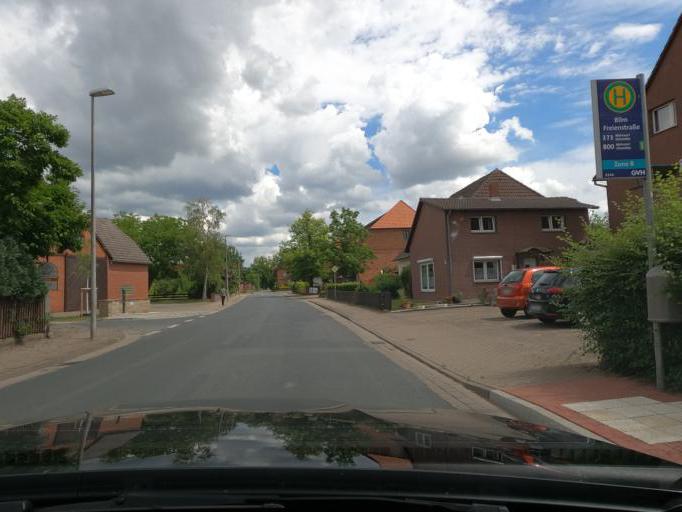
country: DE
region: Lower Saxony
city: Sehnde
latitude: 52.3393
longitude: 9.9130
